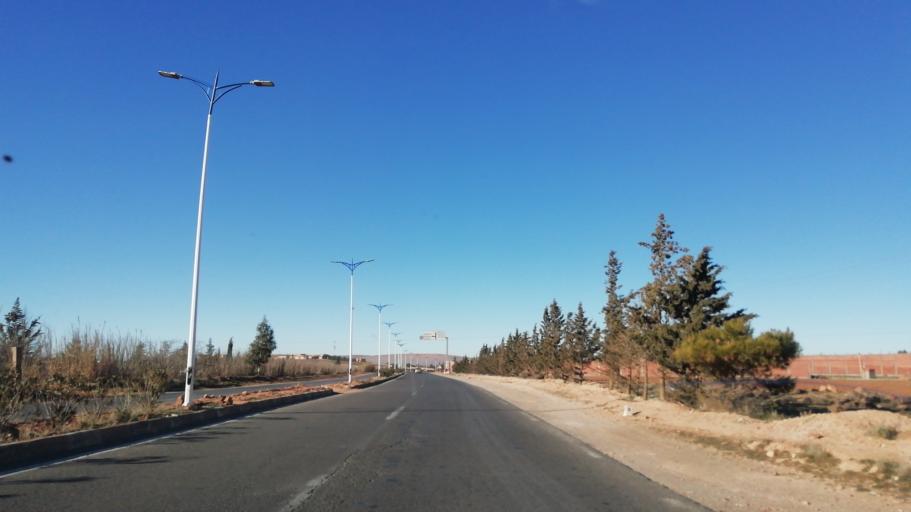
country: DZ
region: El Bayadh
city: El Bayadh
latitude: 33.6883
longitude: 1.0588
